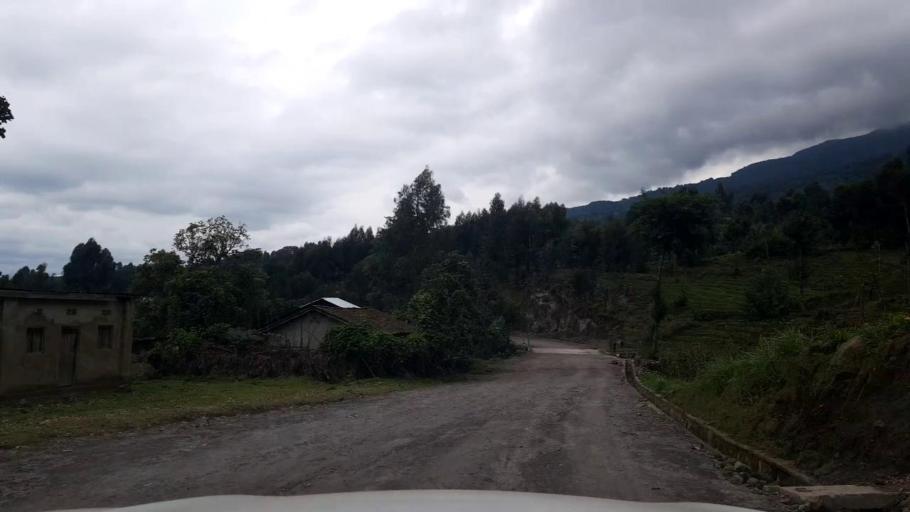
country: RW
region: Northern Province
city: Musanze
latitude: -1.5243
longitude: 29.5317
